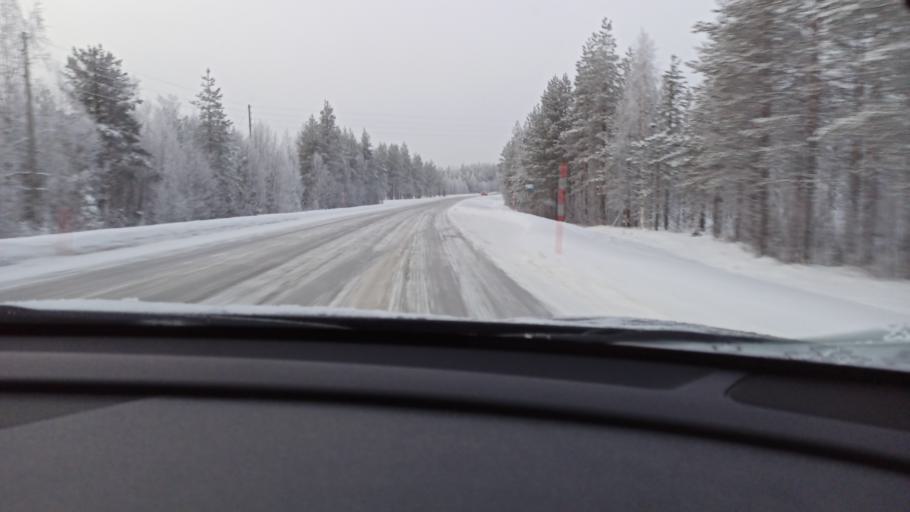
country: FI
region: Lapland
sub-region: Pohjois-Lappi
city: Sodankylae
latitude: 66.9308
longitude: 26.2565
